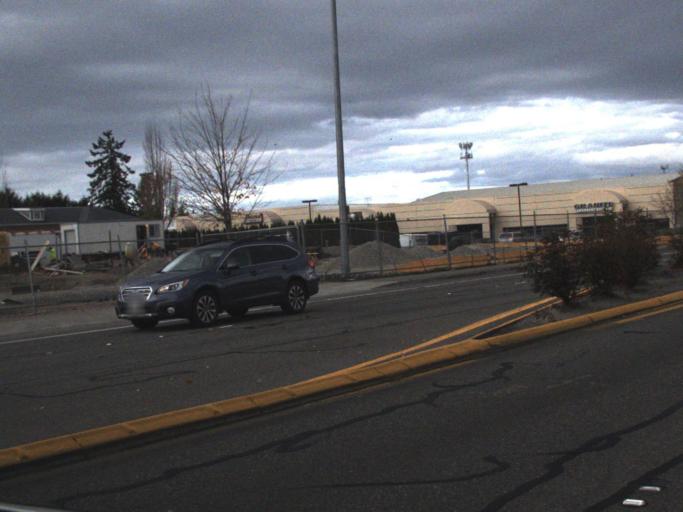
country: US
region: Washington
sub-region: Snohomish County
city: Mukilteo
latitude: 47.8929
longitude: -122.2870
